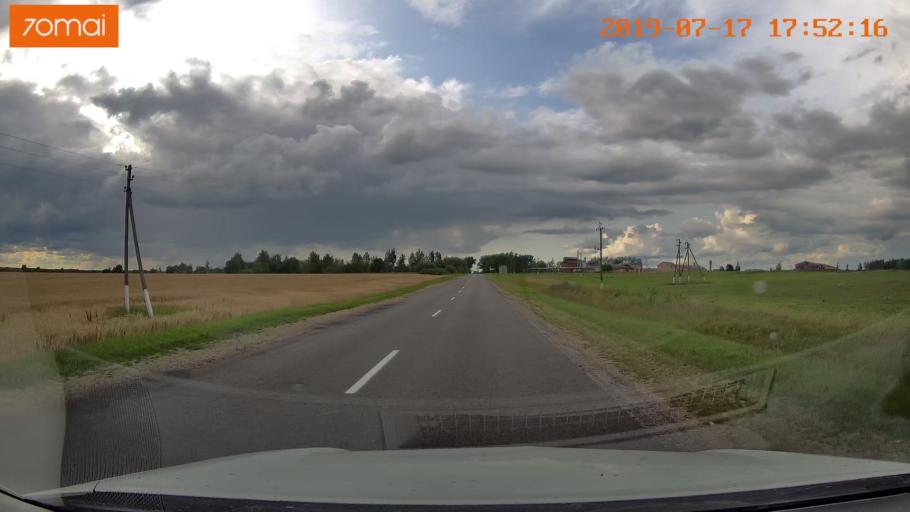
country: BY
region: Mogilev
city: Hlusha
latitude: 53.1632
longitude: 28.7838
